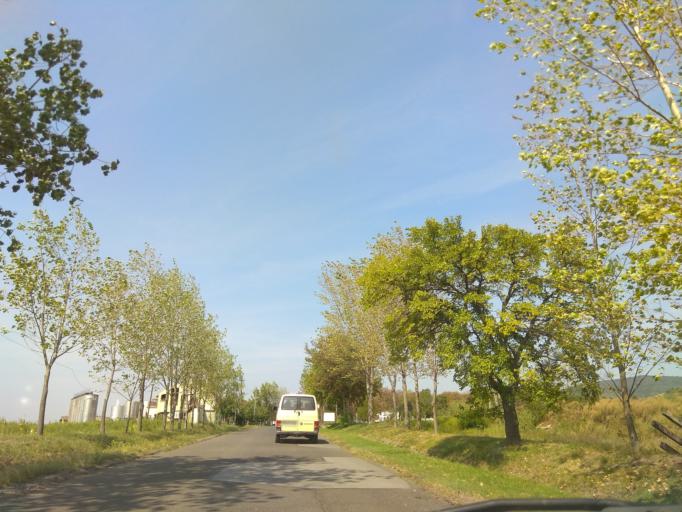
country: HU
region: Borsod-Abauj-Zemplen
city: Tallya
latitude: 48.2286
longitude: 21.2353
